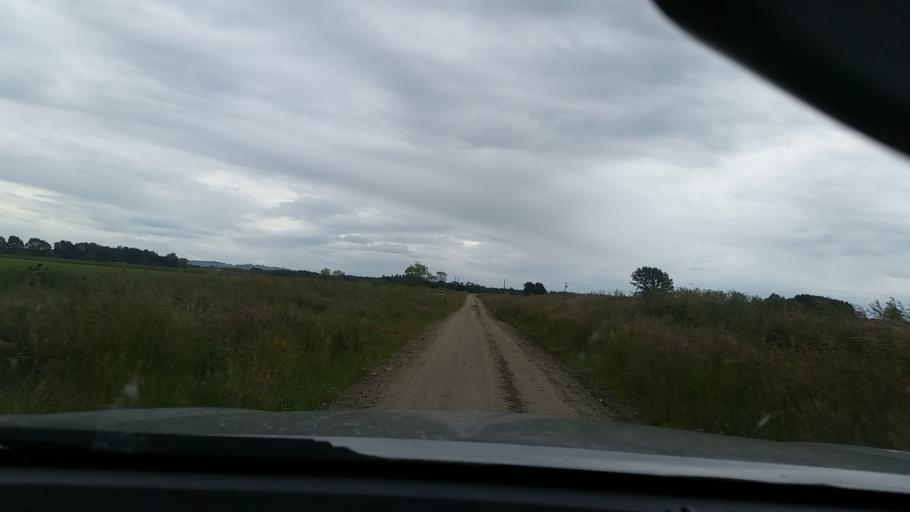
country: NZ
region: Southland
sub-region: Gore District
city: Gore
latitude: -46.2811
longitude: 168.7662
